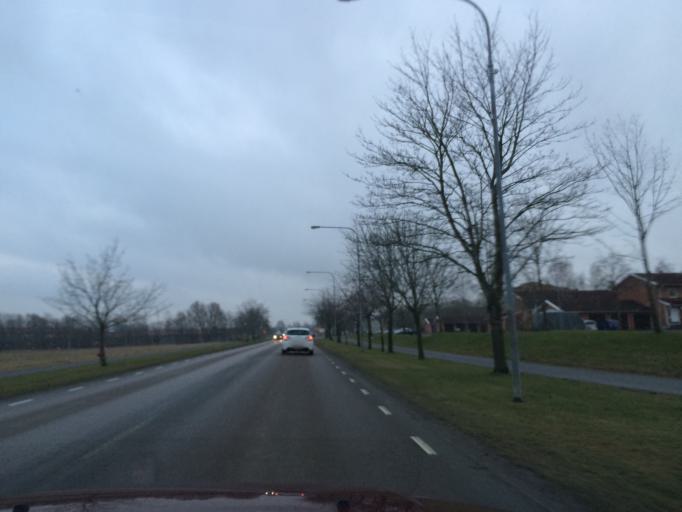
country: SE
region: Halland
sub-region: Kungsbacka Kommun
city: Kungsbacka
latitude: 57.4988
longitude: 12.0702
